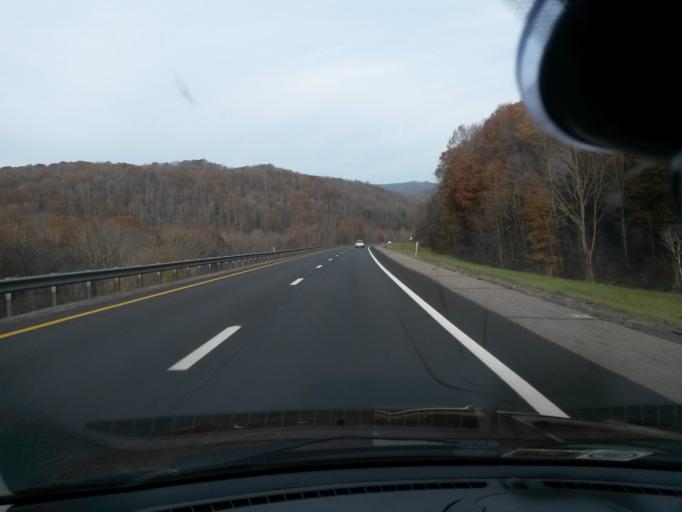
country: US
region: West Virginia
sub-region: Raleigh County
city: Prosperity
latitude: 37.8493
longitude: -81.2477
